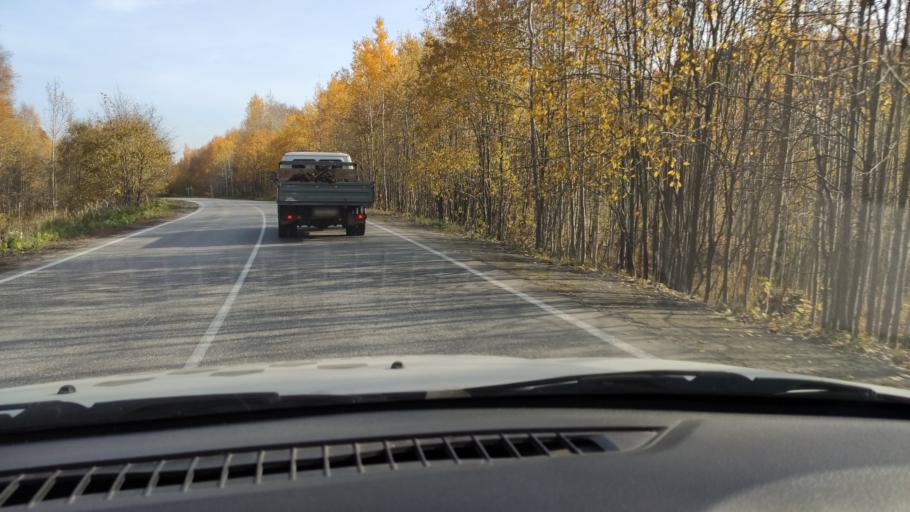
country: RU
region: Perm
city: Novyye Lyady
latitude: 58.0208
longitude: 56.6509
